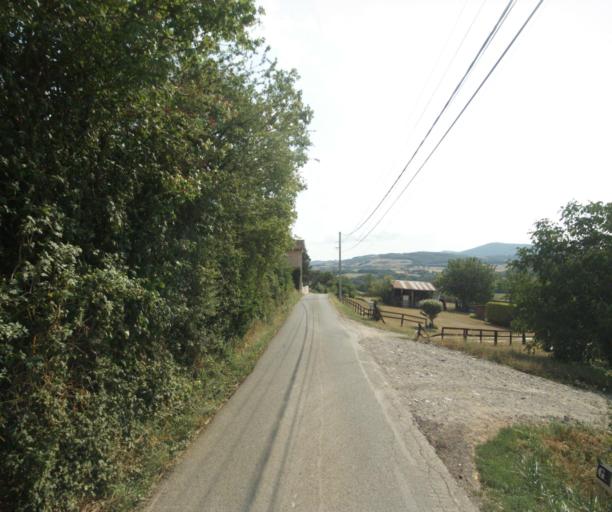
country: FR
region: Rhone-Alpes
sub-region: Departement du Rhone
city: Bully
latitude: 45.8478
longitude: 4.5953
